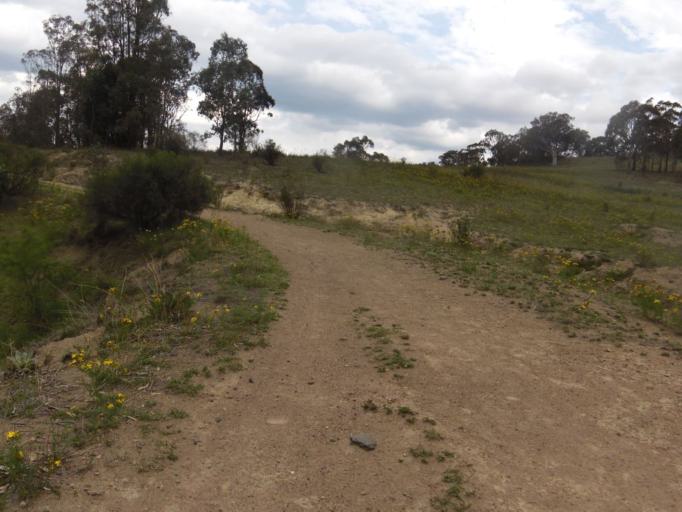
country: AU
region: Australian Capital Territory
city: Forrest
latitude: -35.3566
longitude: 149.1139
